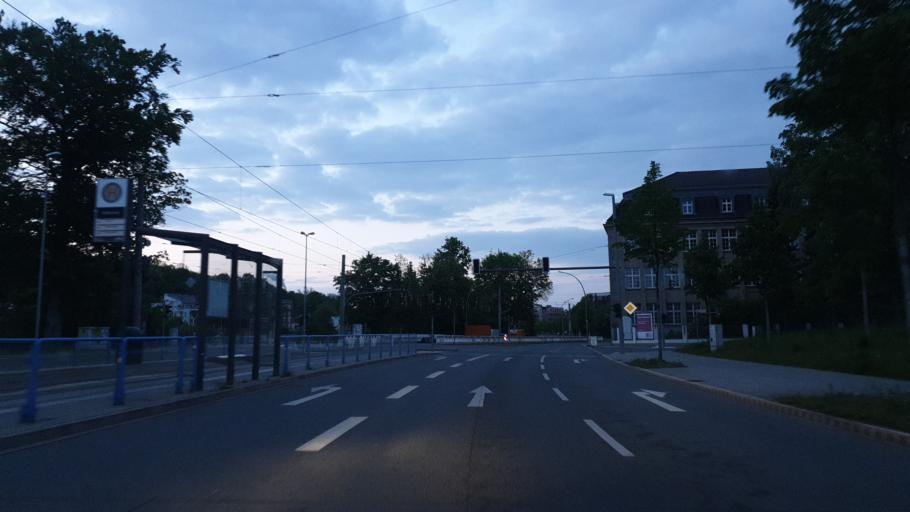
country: DE
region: Saxony
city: Chemnitz
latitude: 50.8193
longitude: 12.9152
